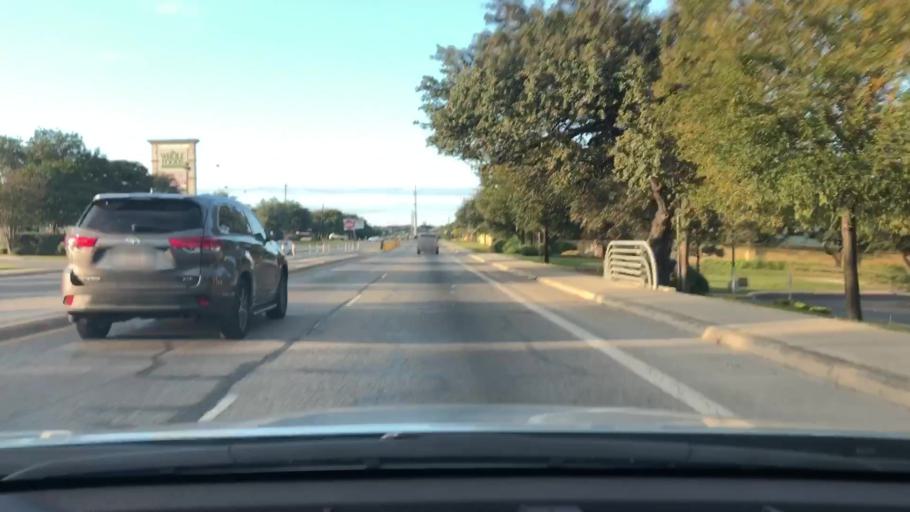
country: US
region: Texas
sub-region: Bexar County
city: Hollywood Park
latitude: 29.6127
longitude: -98.5089
